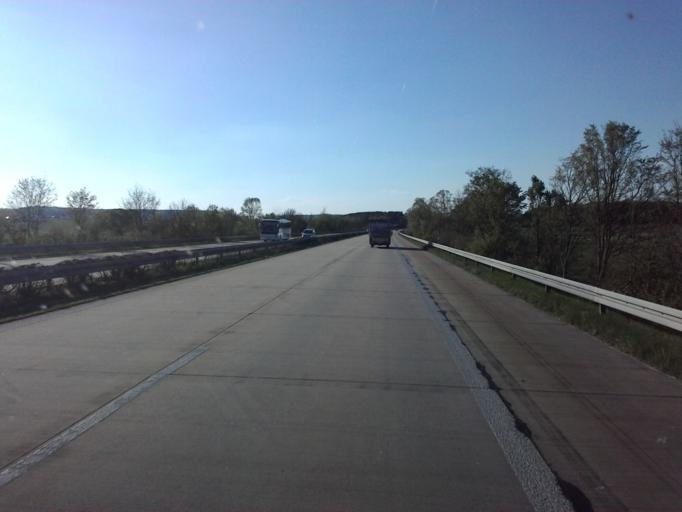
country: DE
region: Bavaria
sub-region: Regierungsbezirk Mittelfranken
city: Schnelldorf
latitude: 49.2187
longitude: 10.2212
